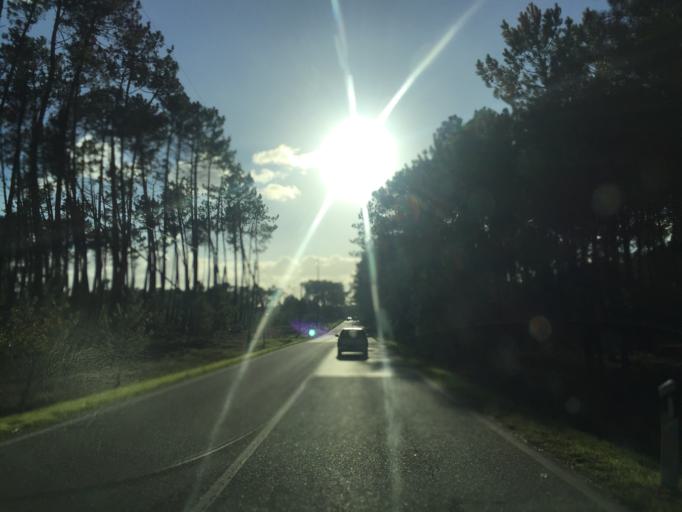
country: PT
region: Leiria
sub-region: Leiria
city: Monte Redondo
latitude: 39.9170
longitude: -8.8135
